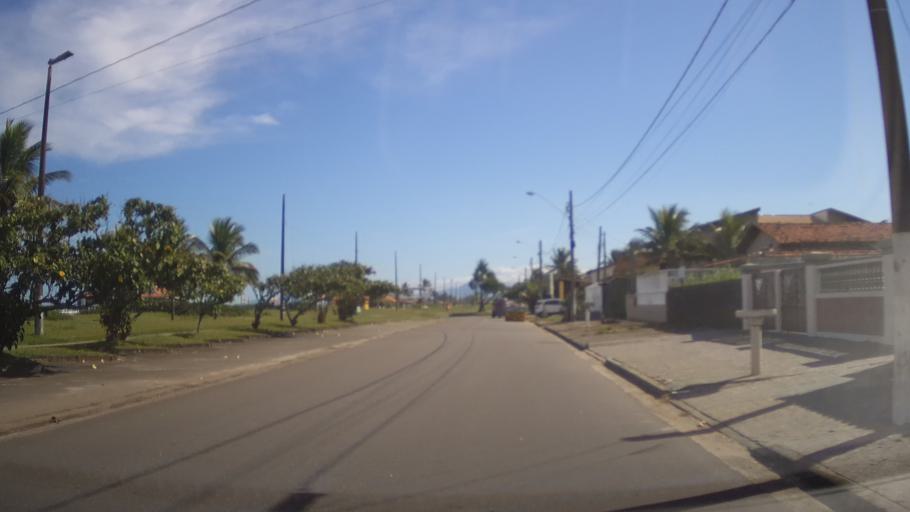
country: BR
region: Sao Paulo
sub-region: Itanhaem
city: Itanhaem
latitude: -24.2066
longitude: -46.8280
